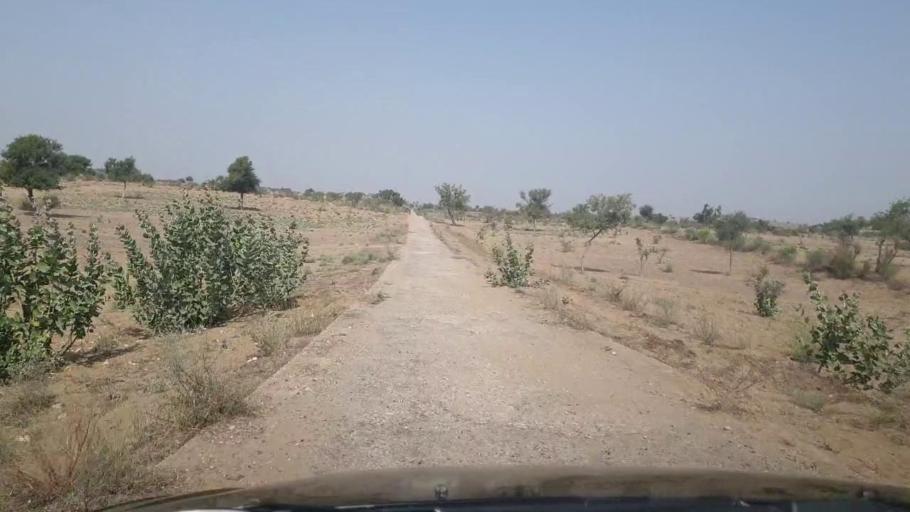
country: PK
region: Sindh
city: Islamkot
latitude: 25.0588
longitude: 70.2093
